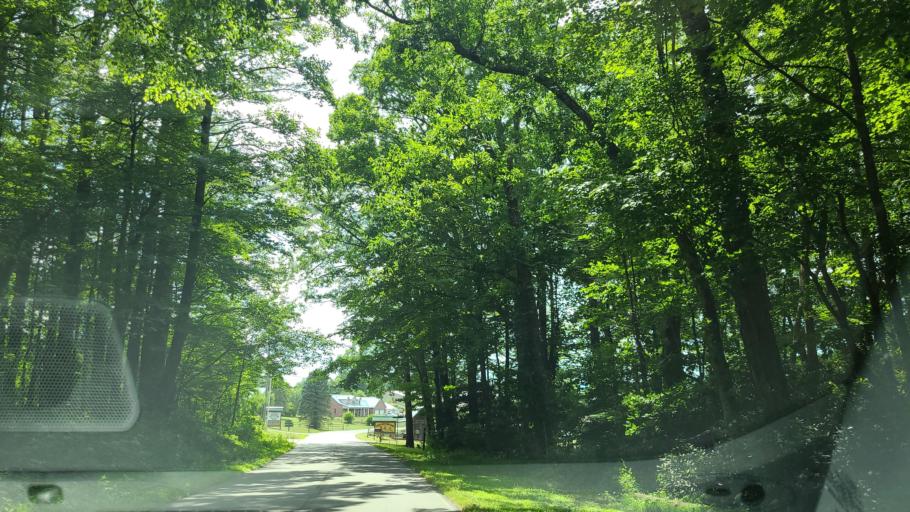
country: US
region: North Carolina
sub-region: Ashe County
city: Jefferson
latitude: 36.3443
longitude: -81.3768
